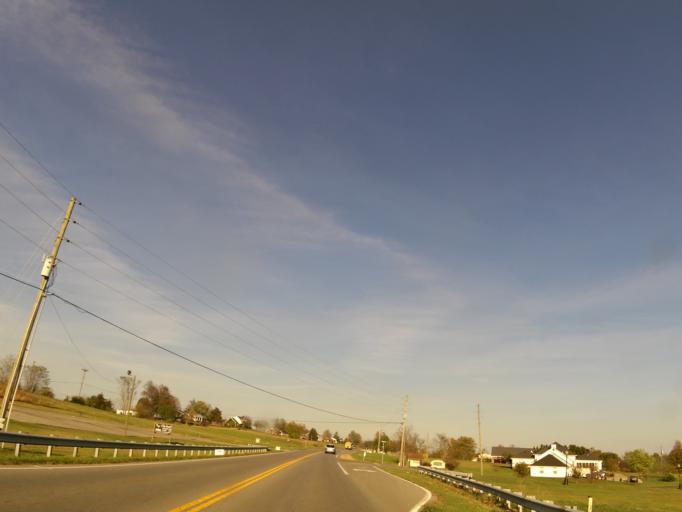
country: US
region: Kentucky
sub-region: Lincoln County
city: Stanford
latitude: 37.5516
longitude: -84.6420
